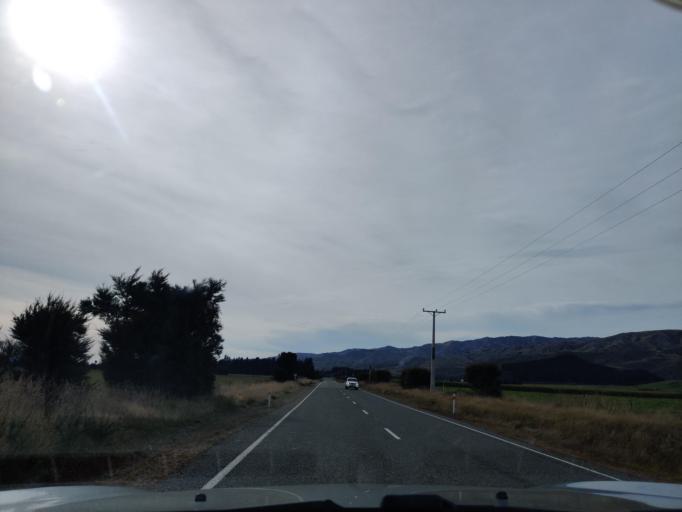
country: NZ
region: Tasman
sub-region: Tasman District
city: Brightwater
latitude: -41.6532
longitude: 173.2599
